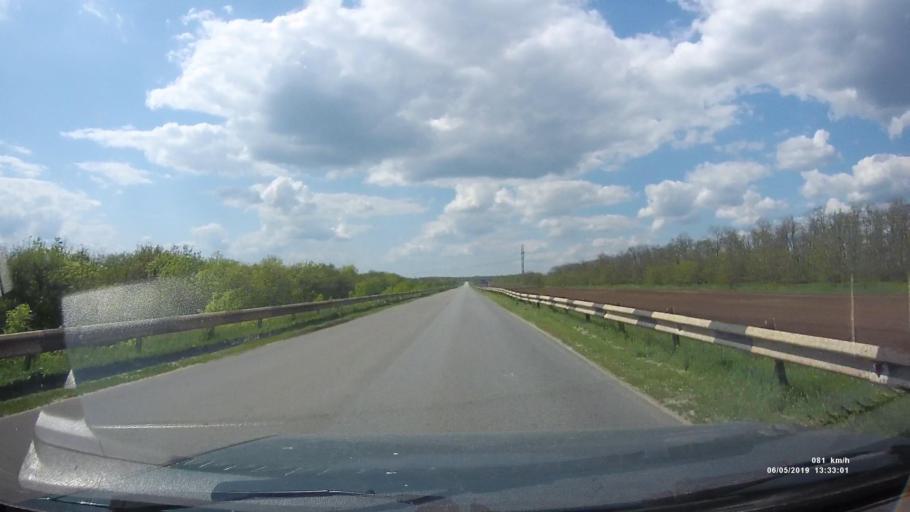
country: RU
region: Rostov
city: Ust'-Donetskiy
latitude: 47.6870
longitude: 40.7859
